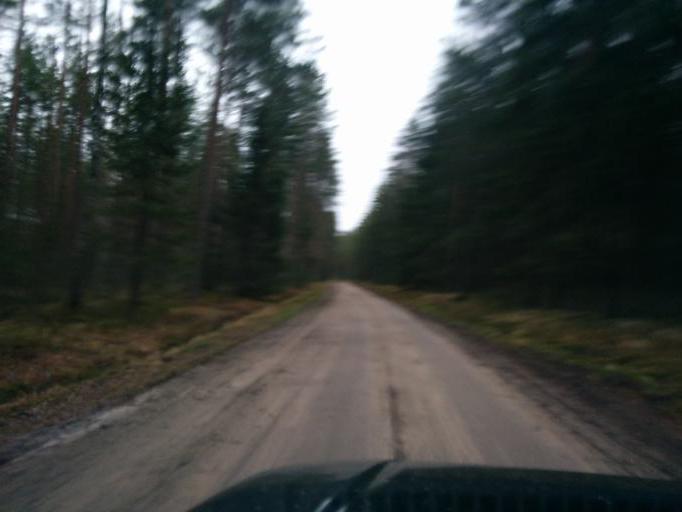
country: LV
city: Tireli
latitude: 56.7993
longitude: 23.6748
